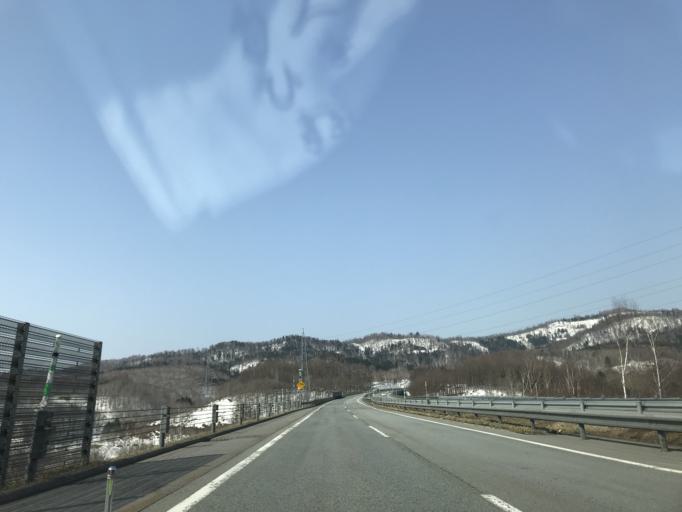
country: JP
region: Hokkaido
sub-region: Asahikawa-shi
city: Asahikawa
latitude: 43.7940
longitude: 142.2832
